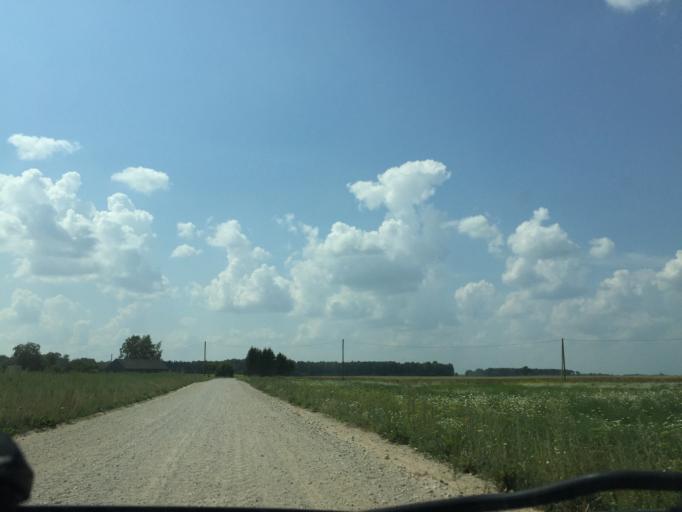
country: LT
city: Zagare
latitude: 56.3965
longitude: 23.2218
